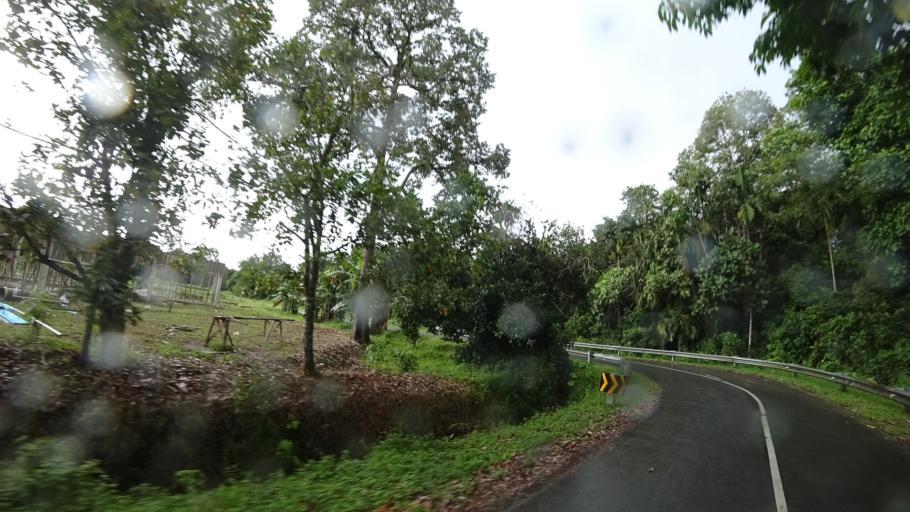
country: BN
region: Brunei and Muara
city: Bandar Seri Begawan
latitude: 4.8278
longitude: 114.9104
